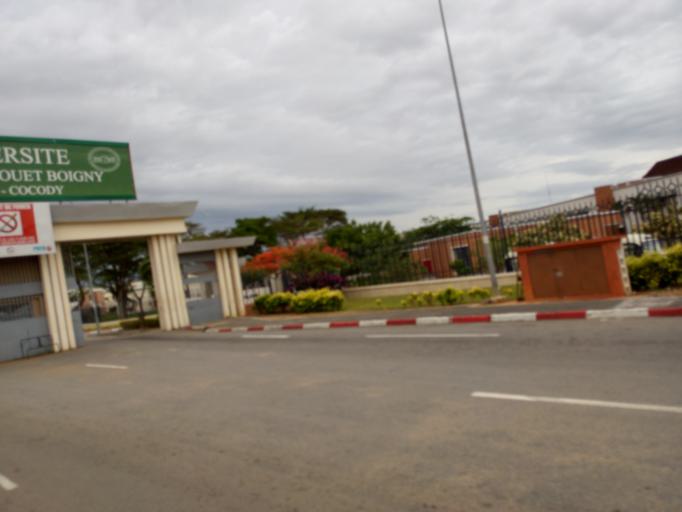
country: CI
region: Lagunes
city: Abidjan
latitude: 5.3499
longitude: -3.9889
